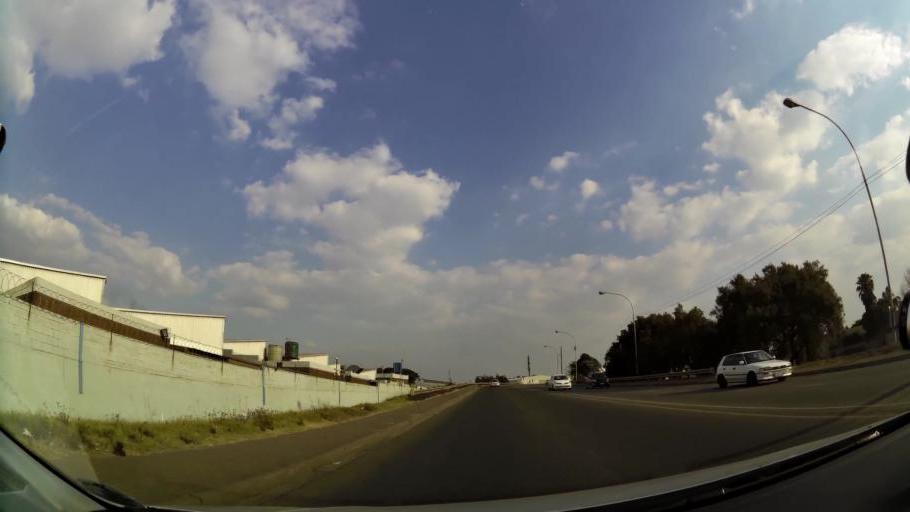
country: ZA
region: Gauteng
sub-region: City of Johannesburg Metropolitan Municipality
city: Modderfontein
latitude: -26.1173
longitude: 28.2082
